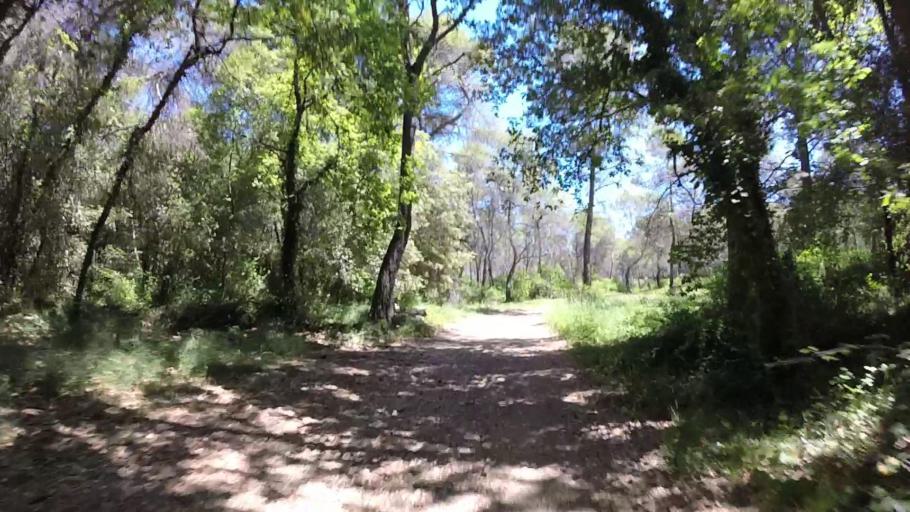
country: FR
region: Provence-Alpes-Cote d'Azur
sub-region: Departement des Alpes-Maritimes
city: Valbonne
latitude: 43.6250
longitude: 7.0187
